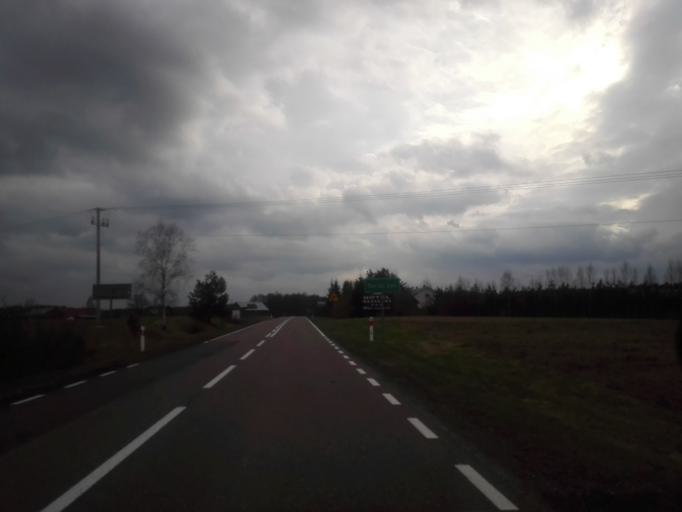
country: PL
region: Podlasie
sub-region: Powiat sejnenski
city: Krasnopol
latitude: 53.9425
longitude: 23.1850
